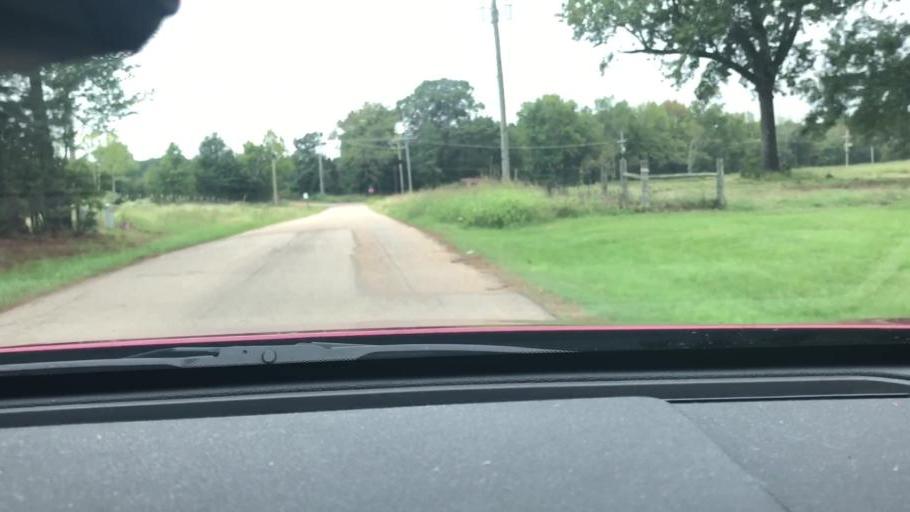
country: US
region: Texas
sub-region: Bowie County
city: Wake Village
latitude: 33.3758
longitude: -94.0977
